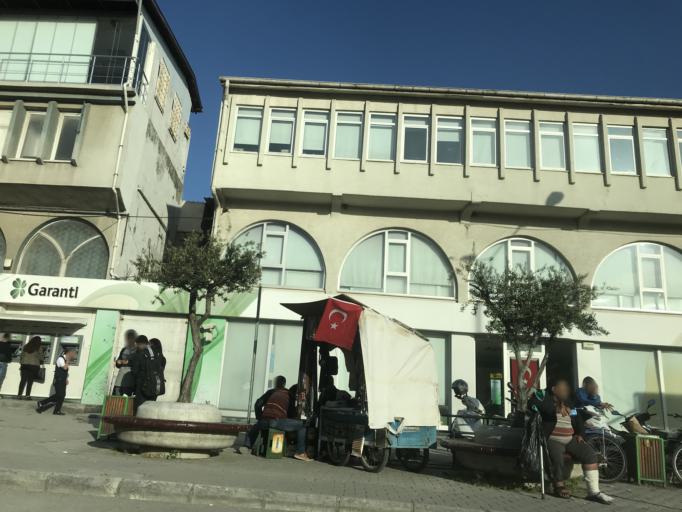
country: TR
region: Hatay
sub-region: Antakya Ilcesi
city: Antakya
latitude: 36.2044
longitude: 36.1623
